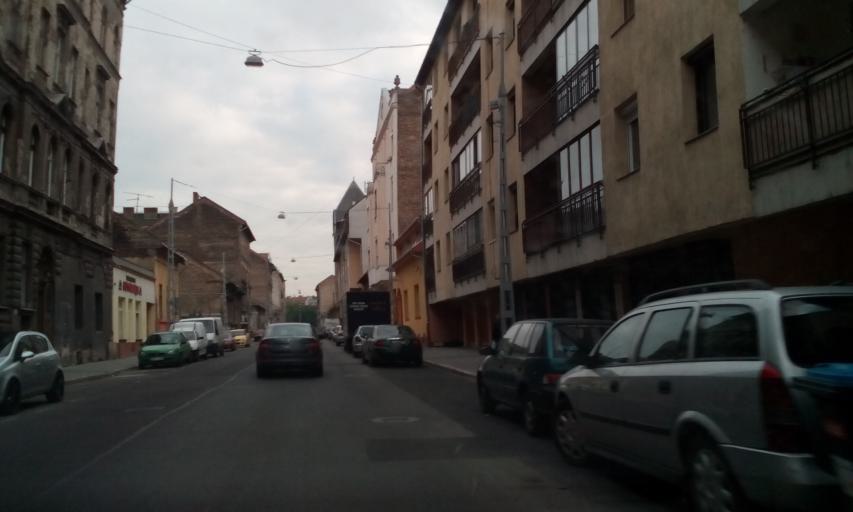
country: HU
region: Budapest
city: Budapest VIII. keruelet
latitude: 47.4920
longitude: 19.0838
